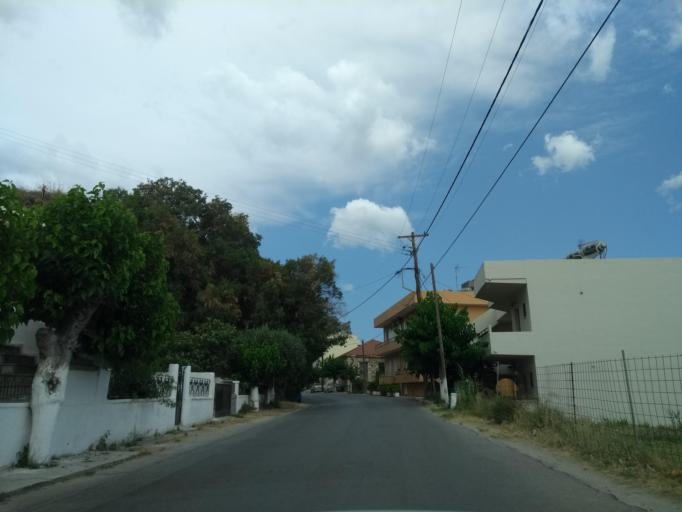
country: GR
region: Crete
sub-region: Nomos Chanias
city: Kalivai
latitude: 35.4572
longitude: 24.1675
